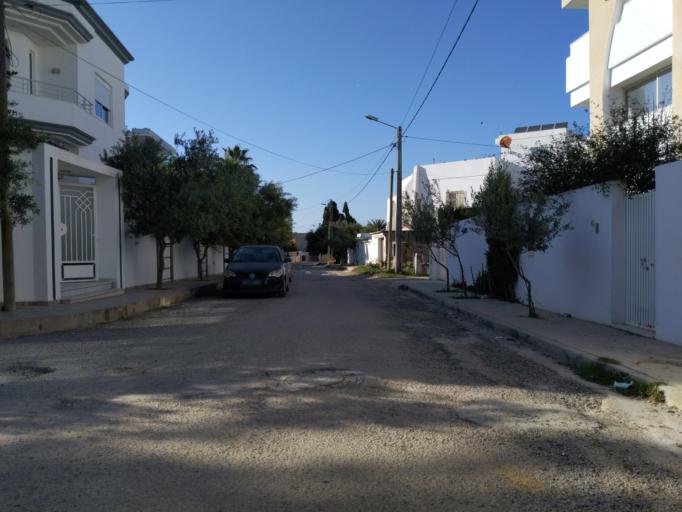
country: TN
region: Al Munastir
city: Saqanis
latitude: 35.7765
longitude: 10.7986
